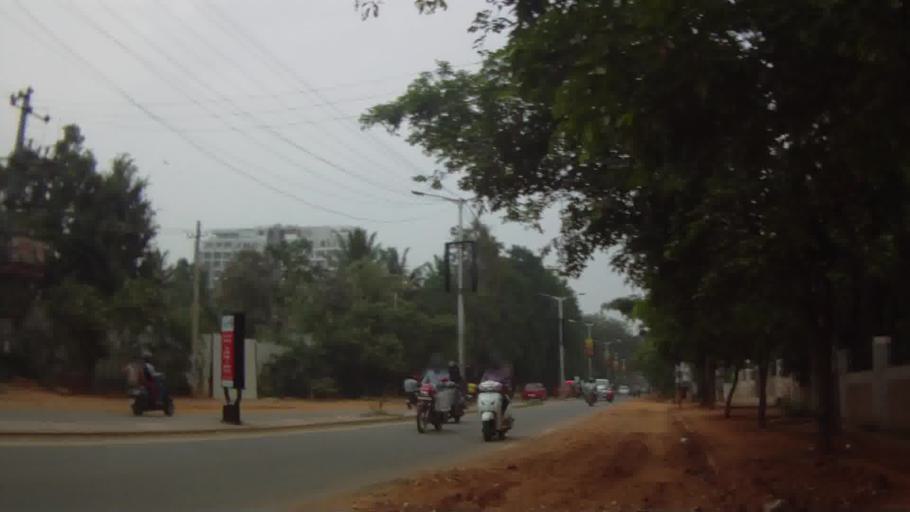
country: IN
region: Karnataka
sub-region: Bangalore Rural
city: Hoskote
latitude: 12.9570
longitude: 77.7363
